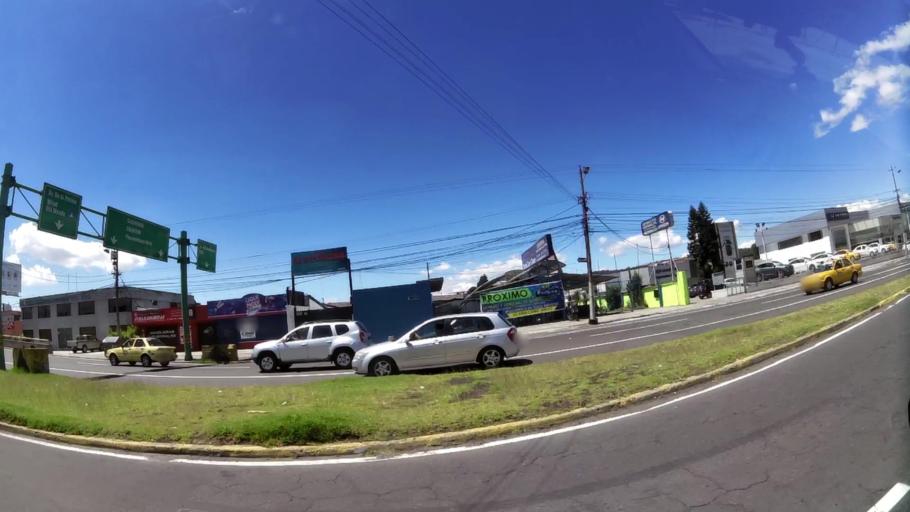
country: EC
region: Pichincha
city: Quito
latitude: -0.1583
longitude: -78.4855
